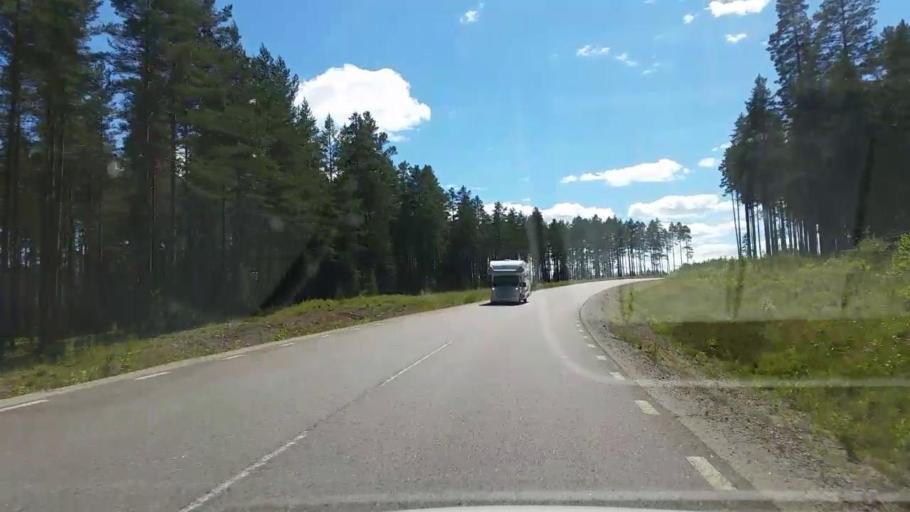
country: SE
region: Dalarna
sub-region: Faluns Kommun
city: Svardsjo
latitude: 61.0360
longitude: 15.7830
